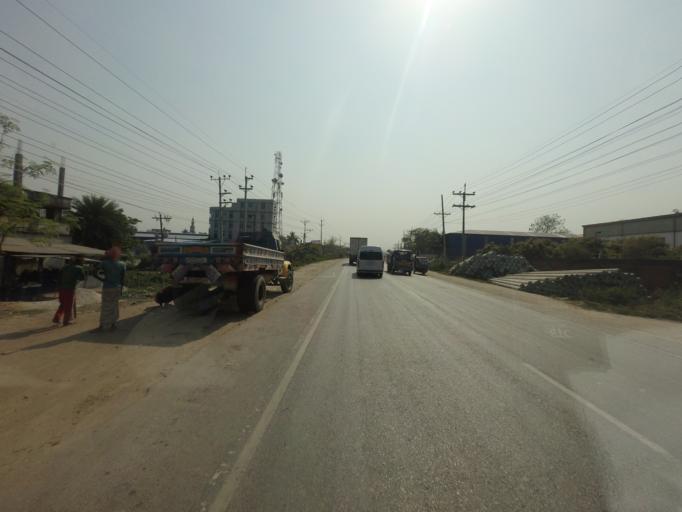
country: BD
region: Dhaka
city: Paltan
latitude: 23.7917
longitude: 90.5766
